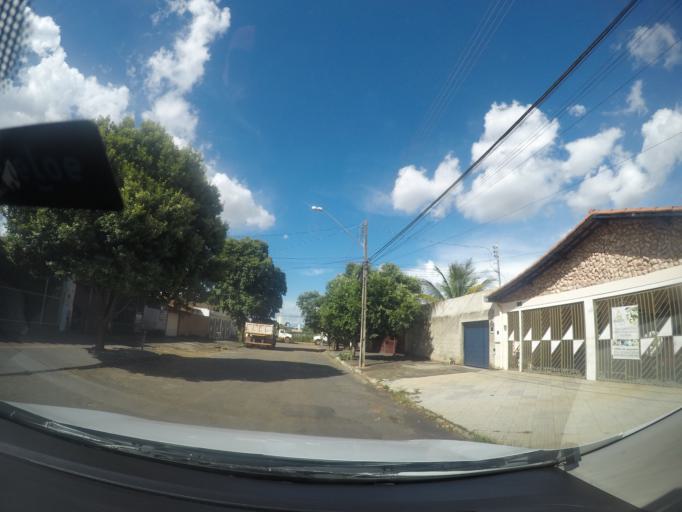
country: BR
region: Goias
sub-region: Goiania
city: Goiania
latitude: -16.6784
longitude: -49.2992
